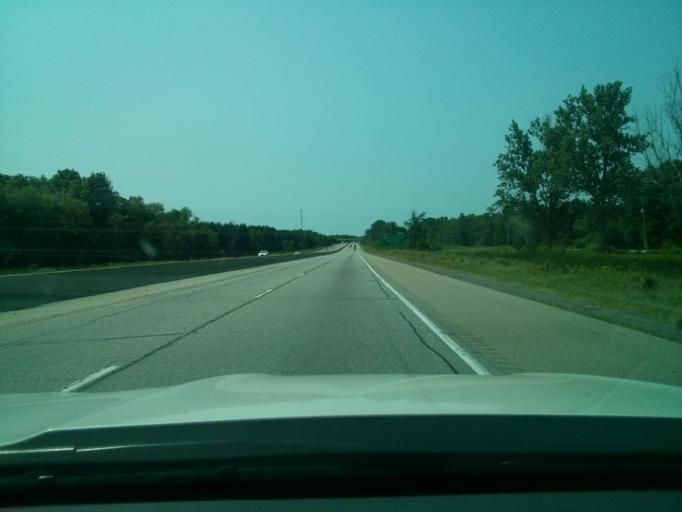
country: CA
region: Ontario
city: Brockville
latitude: 44.6602
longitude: -75.6175
